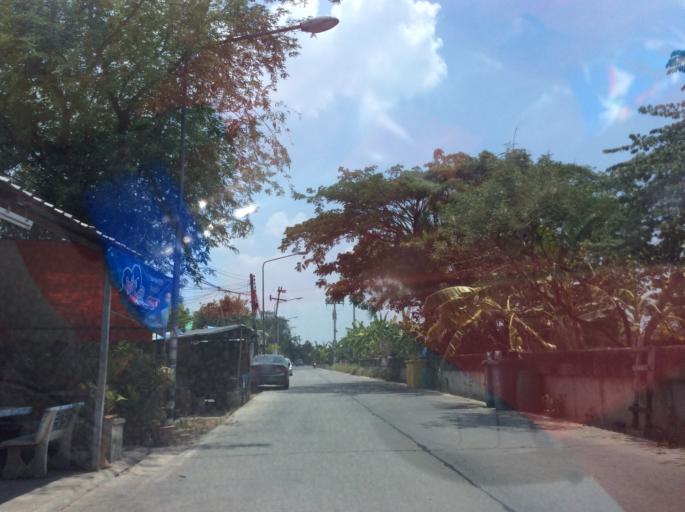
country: TH
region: Pathum Thani
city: Thanyaburi
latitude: 14.0211
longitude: 100.7382
